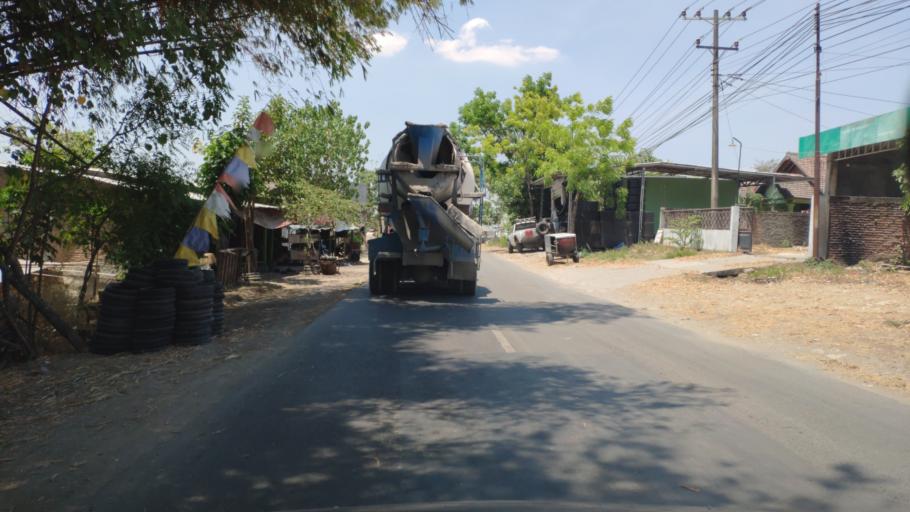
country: ID
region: Central Java
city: Cepu
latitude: -7.1362
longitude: 111.5798
